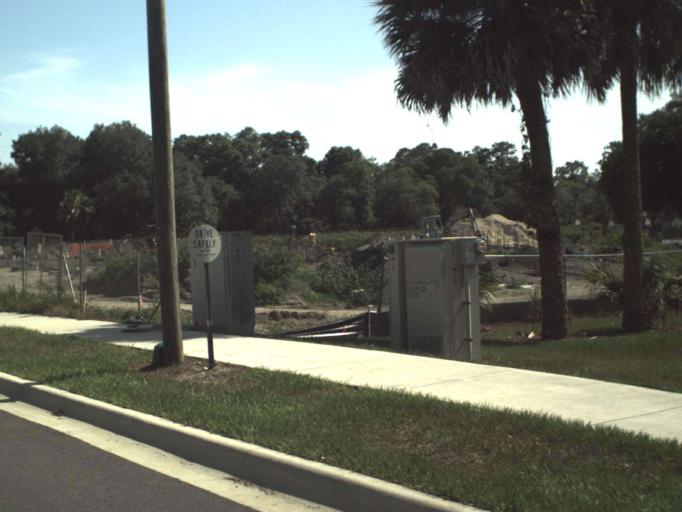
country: US
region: Florida
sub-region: Seminole County
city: Oviedo
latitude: 28.6604
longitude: -81.2083
